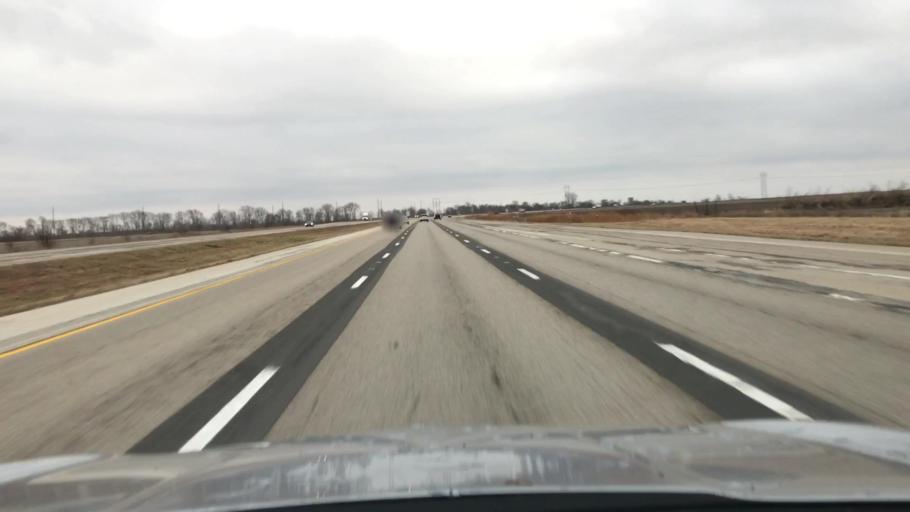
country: US
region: Illinois
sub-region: Logan County
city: Lincoln
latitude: 40.1076
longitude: -89.4165
